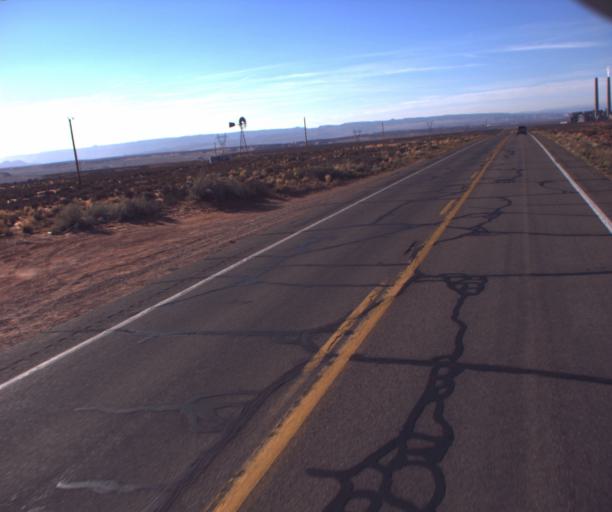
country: US
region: Arizona
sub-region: Coconino County
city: LeChee
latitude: 36.8849
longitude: -111.3578
